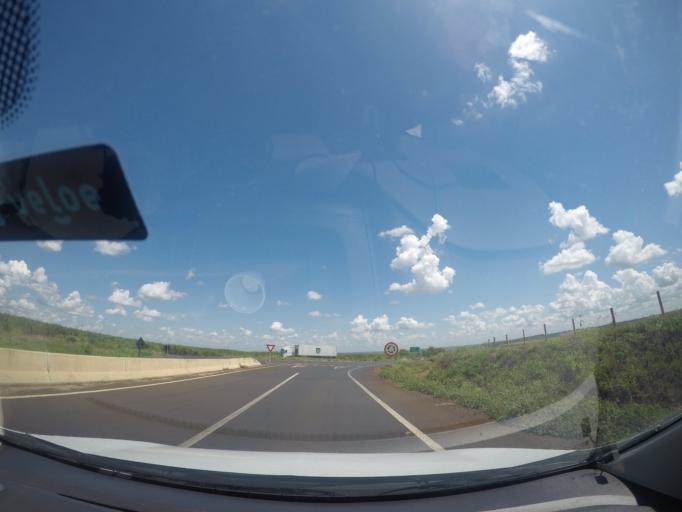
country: BR
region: Minas Gerais
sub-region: Frutal
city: Frutal
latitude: -19.6999
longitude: -48.7654
